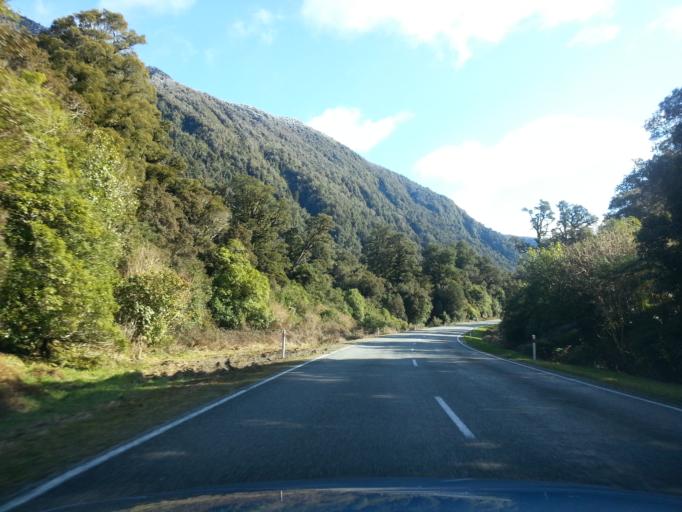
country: NZ
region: West Coast
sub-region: Grey District
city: Greymouth
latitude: -42.7435
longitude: 171.4929
